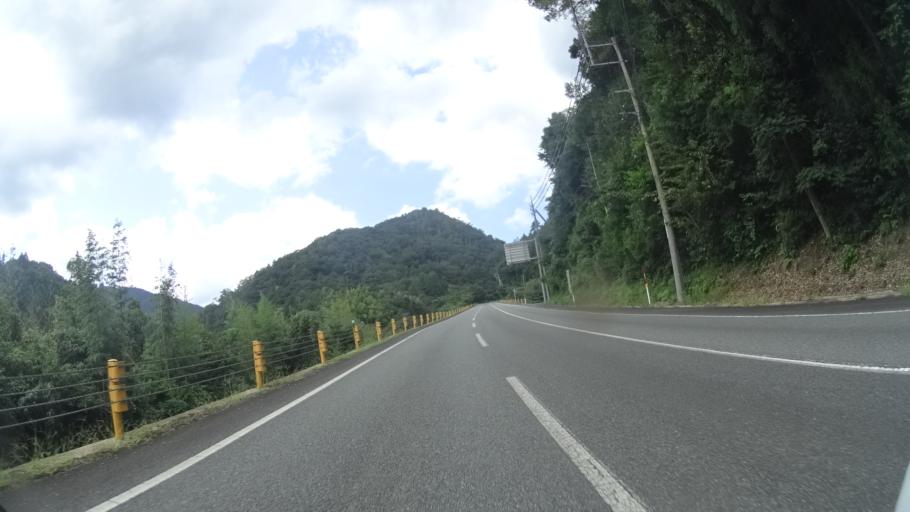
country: JP
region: Yamaguchi
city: Hagi
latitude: 34.5492
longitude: 131.6189
